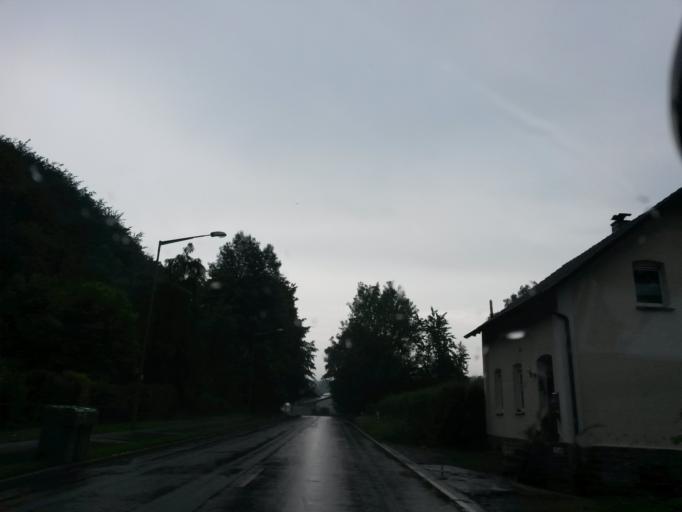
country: DE
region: North Rhine-Westphalia
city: Wiehl
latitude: 50.9882
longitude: 7.5096
